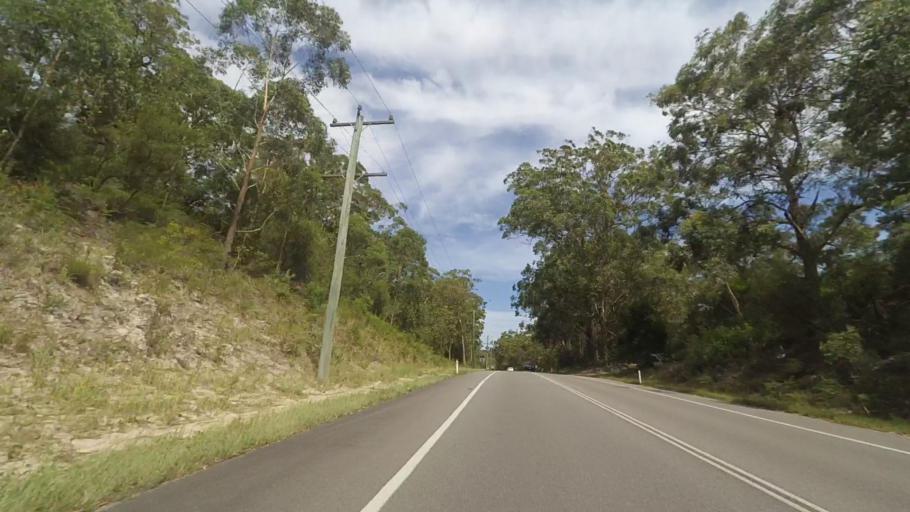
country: AU
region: New South Wales
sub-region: Port Stephens Shire
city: Medowie
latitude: -32.7914
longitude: 151.9396
